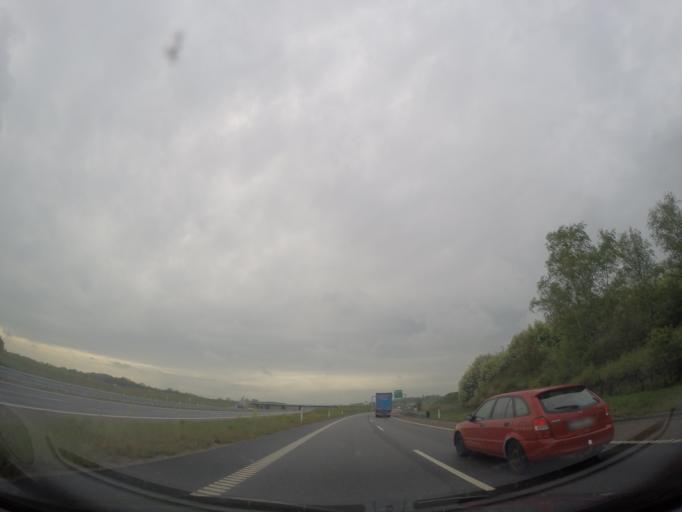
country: DK
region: Capital Region
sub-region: Ballerup Kommune
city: Ballerup
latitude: 55.7013
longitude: 12.3732
